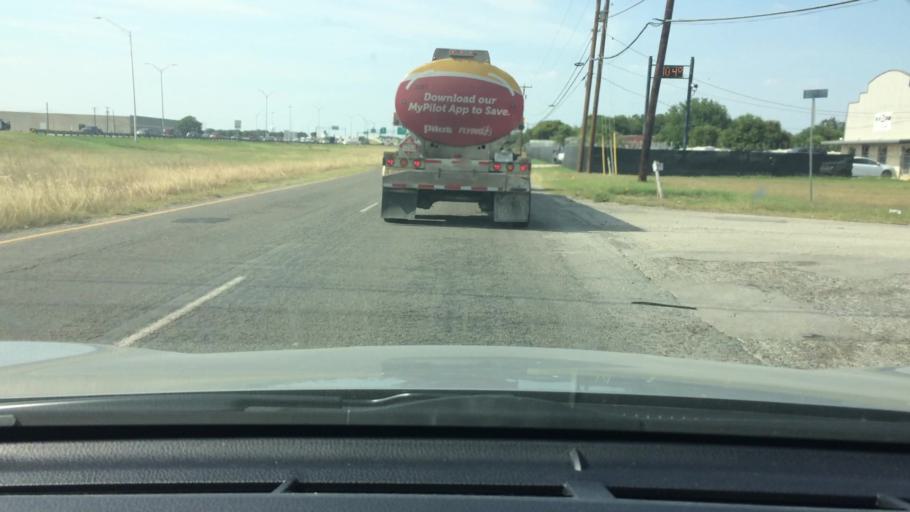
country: US
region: Texas
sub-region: Bexar County
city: Kirby
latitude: 29.4277
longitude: -98.3886
